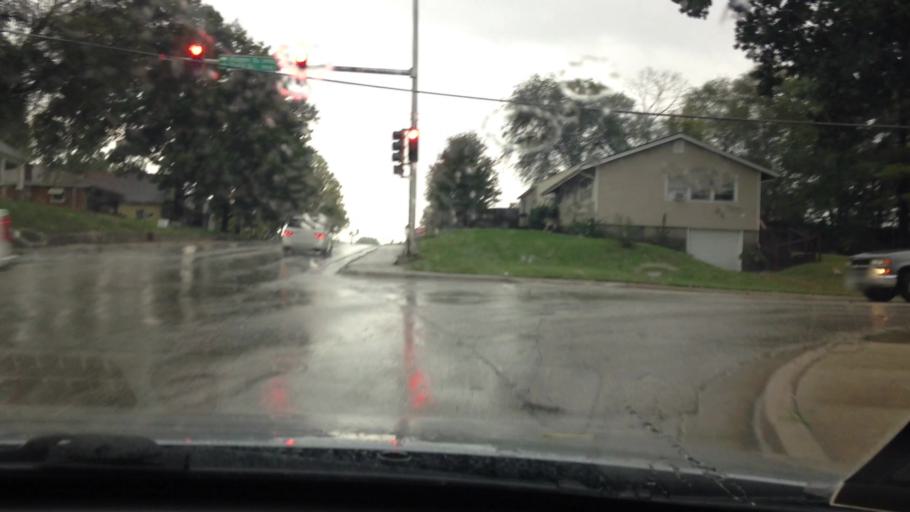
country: US
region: Kansas
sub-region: Leavenworth County
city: Leavenworth
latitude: 39.2886
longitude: -94.9093
